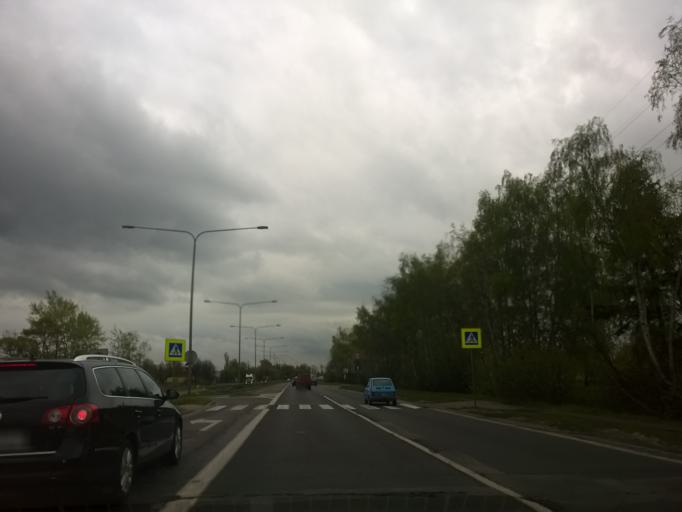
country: PL
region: Masovian Voivodeship
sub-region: Warszawa
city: Kabaty
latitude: 52.1188
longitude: 21.1025
